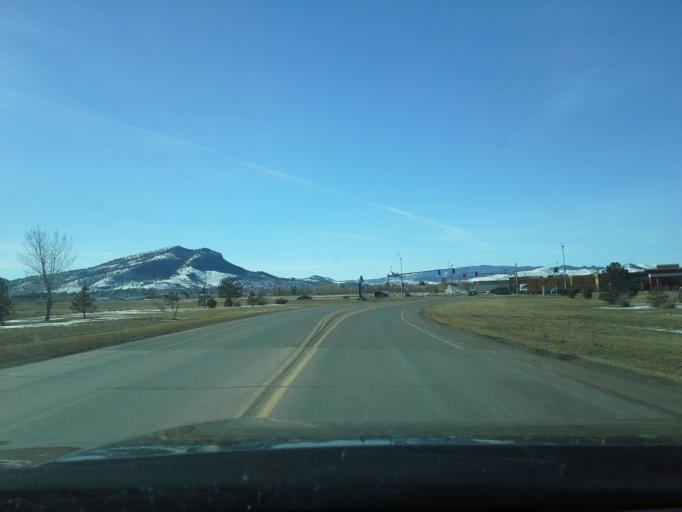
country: US
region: Montana
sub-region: Lewis and Clark County
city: Helena
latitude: 46.6130
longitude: -112.0023
